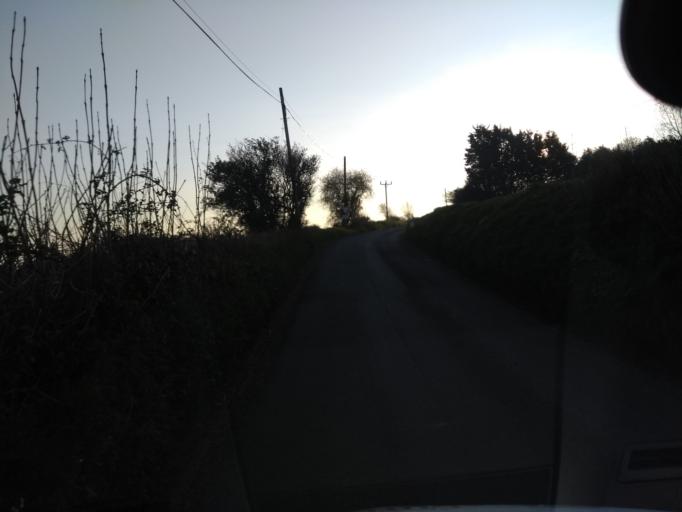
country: GB
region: England
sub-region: Somerset
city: Crewkerne
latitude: 50.8373
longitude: -2.8599
